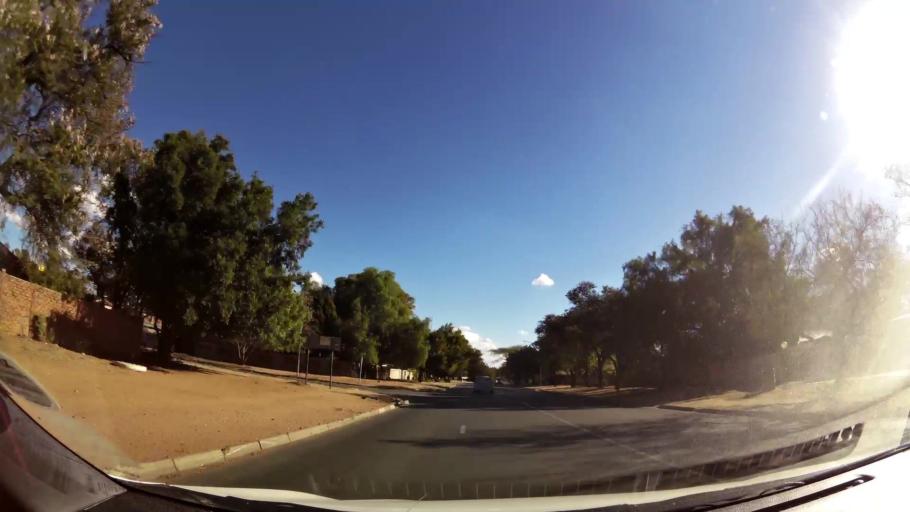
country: ZA
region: Limpopo
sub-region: Capricorn District Municipality
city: Polokwane
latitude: -23.9127
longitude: 29.4821
